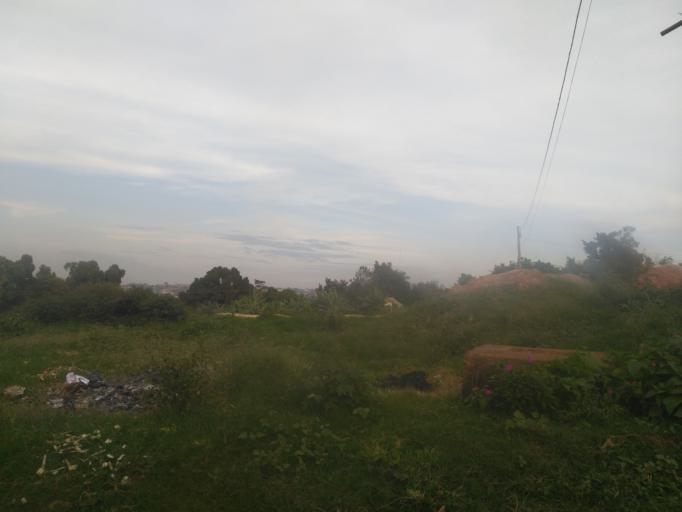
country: UG
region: Central Region
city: Kampala Central Division
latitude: 0.3427
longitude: 32.5796
